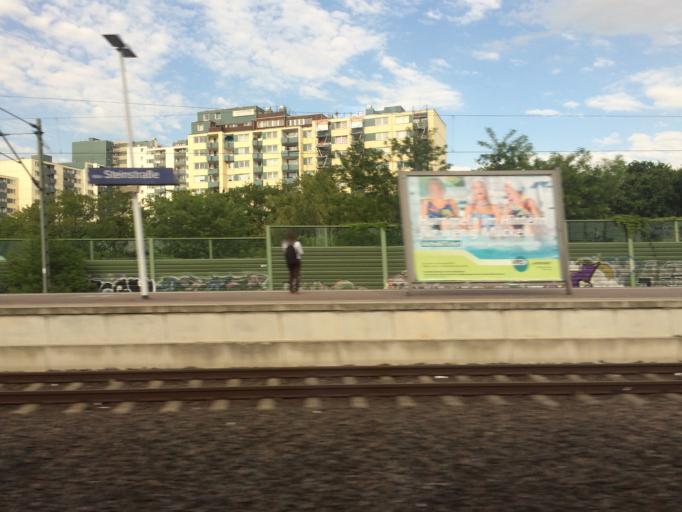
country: DE
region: North Rhine-Westphalia
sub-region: Regierungsbezirk Koln
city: Gremberghoven
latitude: 50.8954
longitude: 7.0571
